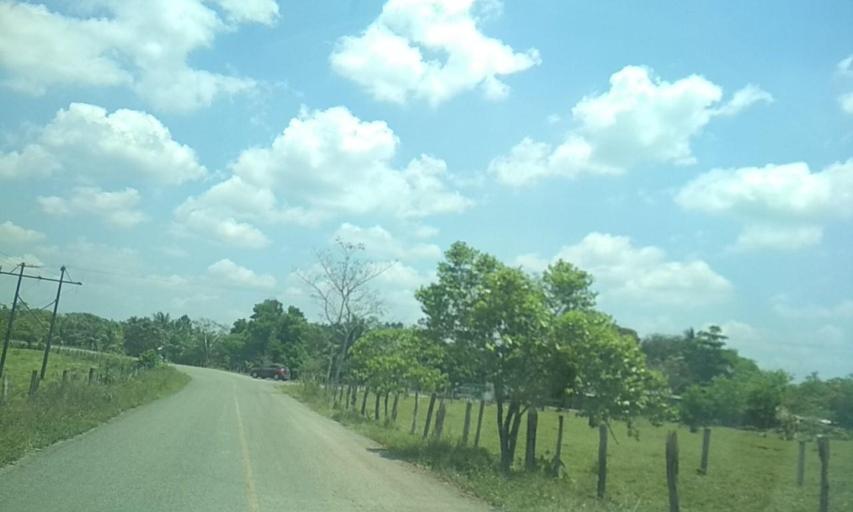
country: MX
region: Tabasco
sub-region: Huimanguillo
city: Francisco Rueda
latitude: 17.7924
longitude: -93.8507
